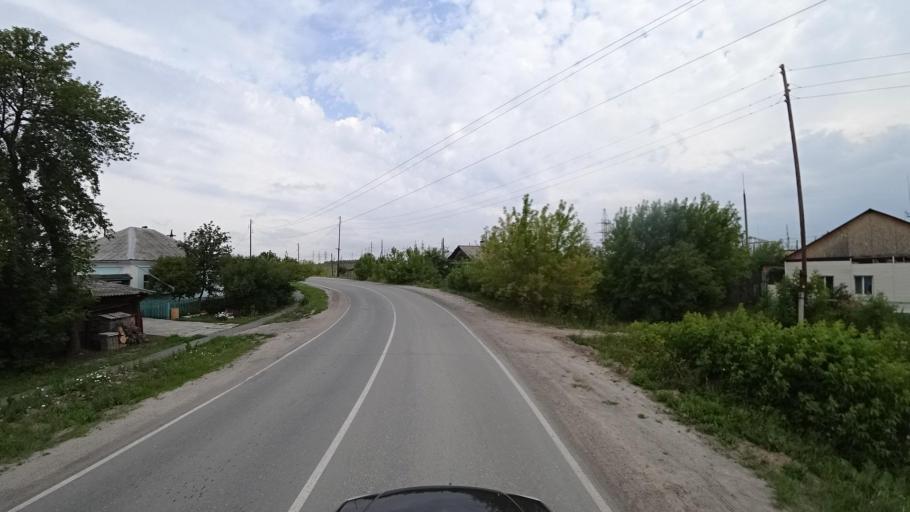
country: RU
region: Sverdlovsk
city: Kamyshlov
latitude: 56.8501
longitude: 62.7427
